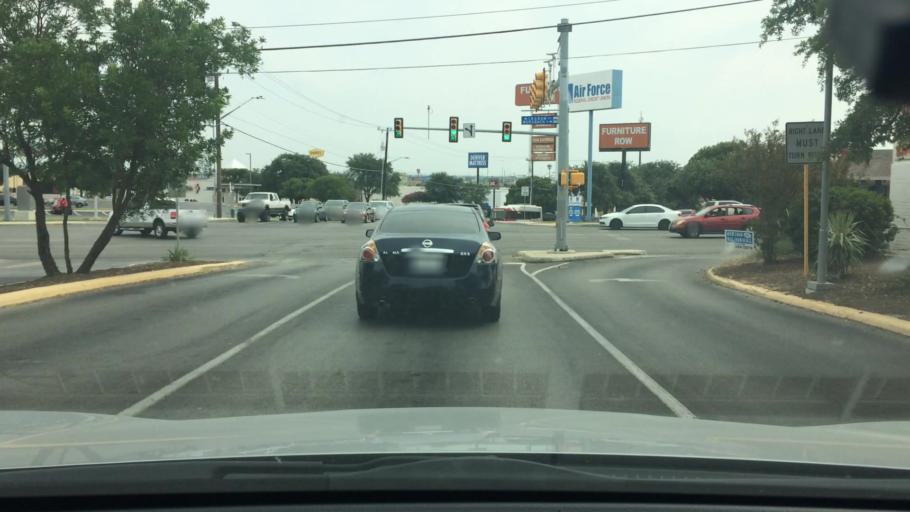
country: US
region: Texas
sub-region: Bexar County
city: Leon Valley
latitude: 29.4665
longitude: -98.6218
